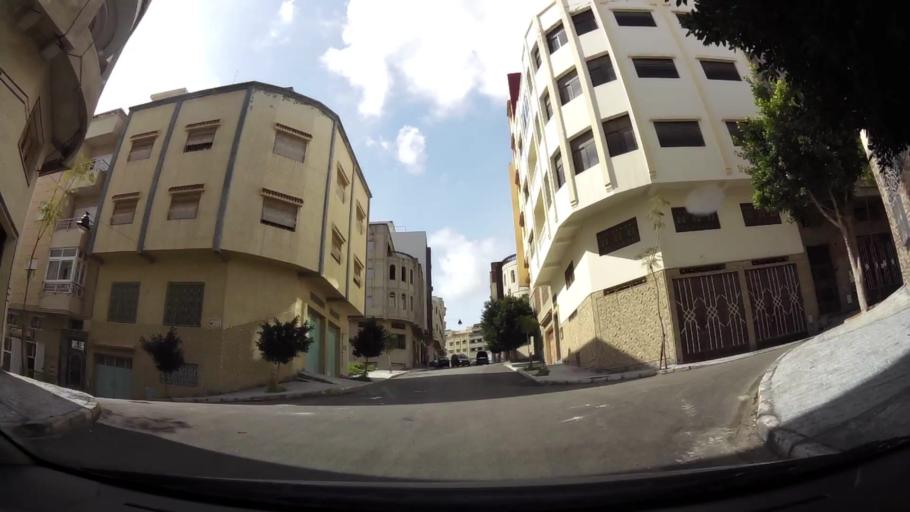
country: MA
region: Tanger-Tetouan
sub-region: Tanger-Assilah
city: Tangier
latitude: 35.7684
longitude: -5.7645
